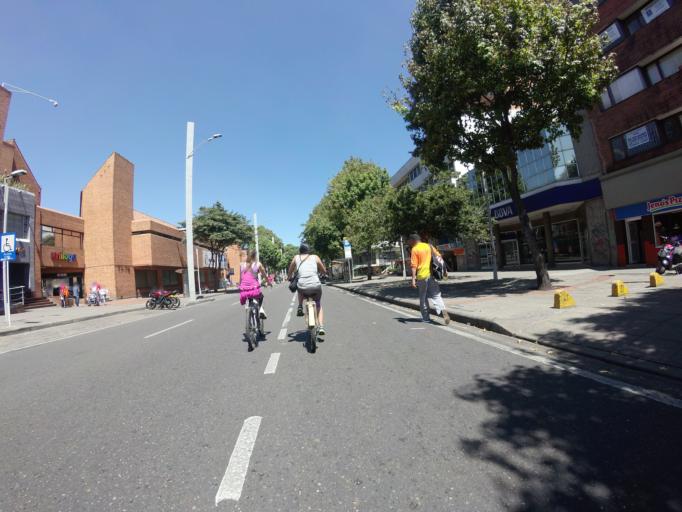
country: CO
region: Bogota D.C.
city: Barrio San Luis
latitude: 4.6643
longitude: -74.0583
